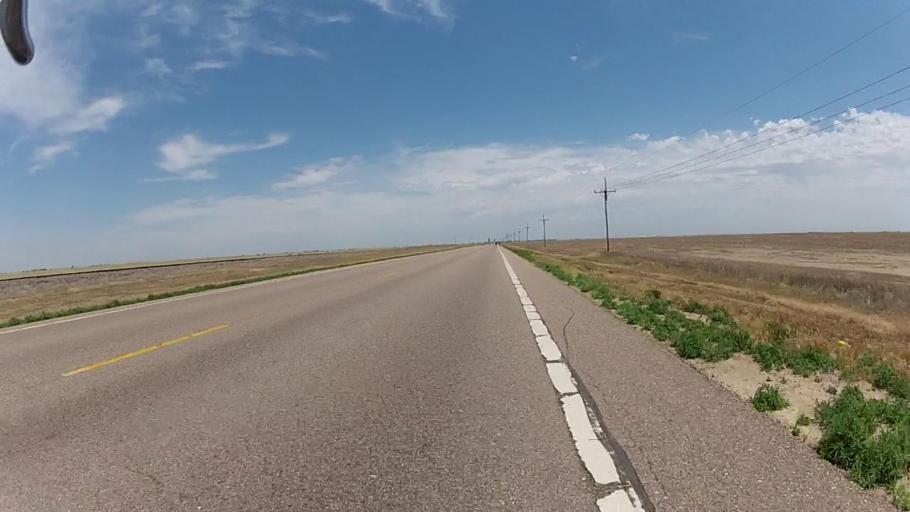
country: US
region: Kansas
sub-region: Haskell County
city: Satanta
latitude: 37.4612
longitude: -100.9227
